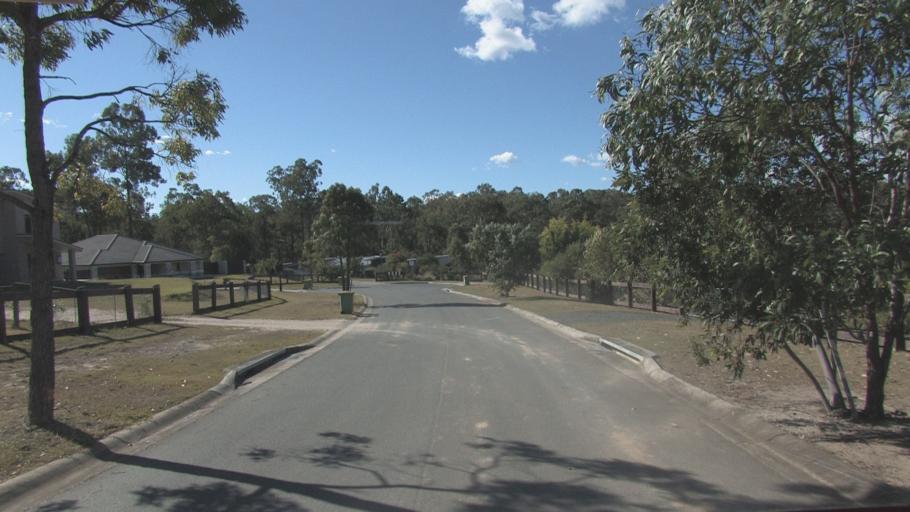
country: AU
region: Queensland
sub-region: Ipswich
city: Springfield Lakes
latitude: -27.7292
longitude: 152.9150
